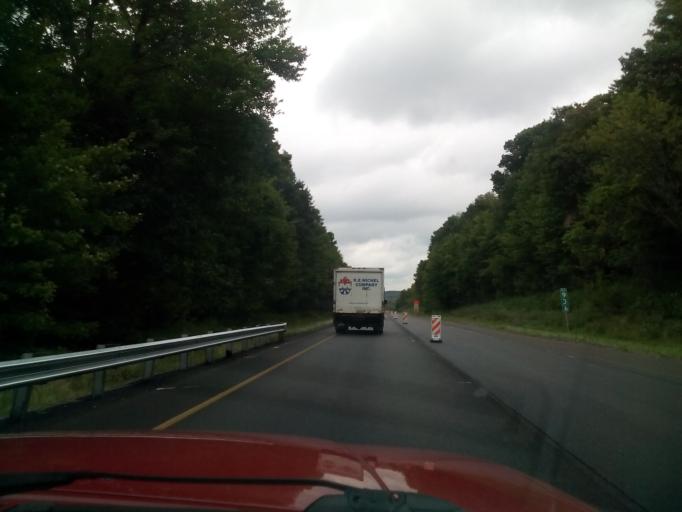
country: US
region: Pennsylvania
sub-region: Jefferson County
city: Falls Creek
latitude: 41.1533
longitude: -78.8411
